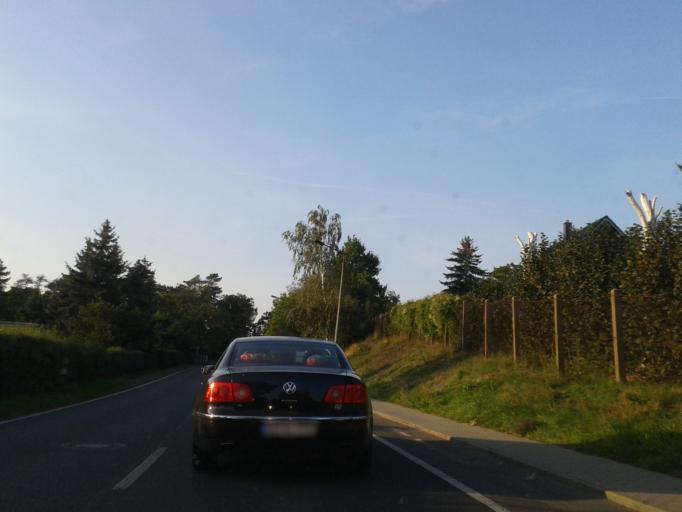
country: DE
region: Saxony
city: Meissen
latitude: 51.1498
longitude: 13.4746
